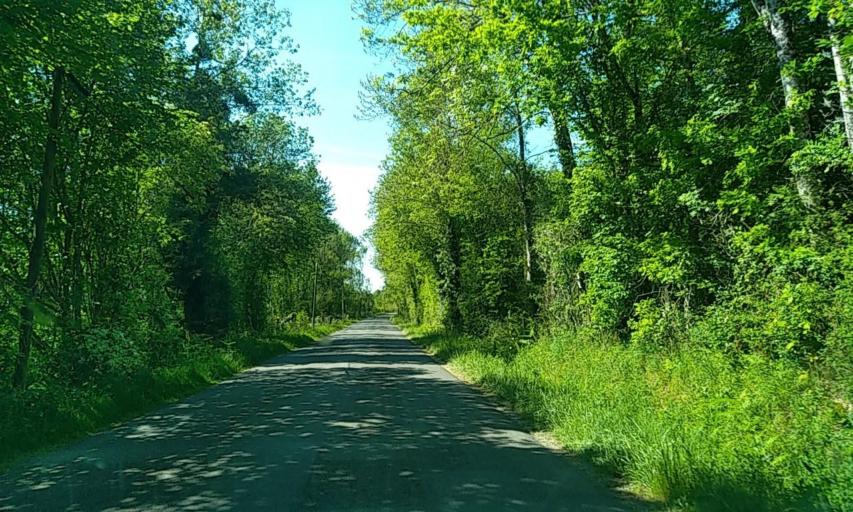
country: FR
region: Poitou-Charentes
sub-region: Departement des Deux-Sevres
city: Boisme
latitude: 46.7827
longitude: -0.4487
